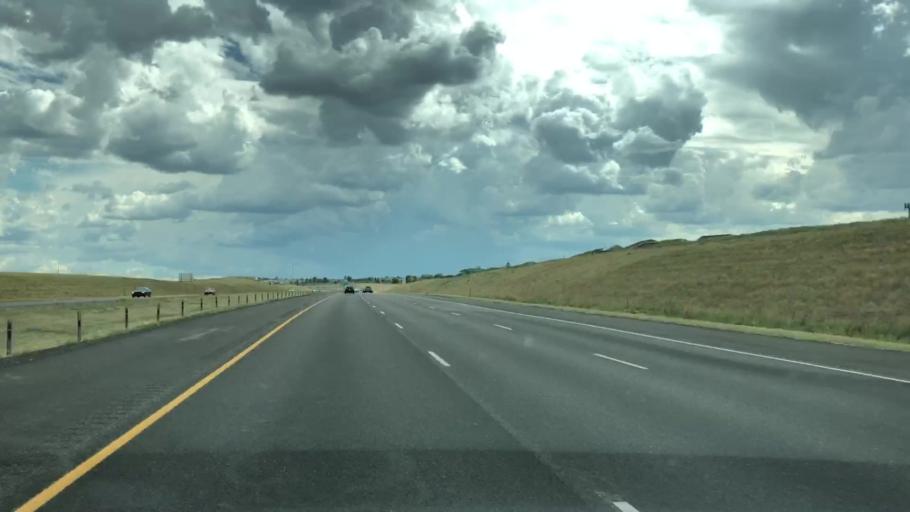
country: US
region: Colorado
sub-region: Douglas County
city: Parker
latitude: 39.6323
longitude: -104.7193
